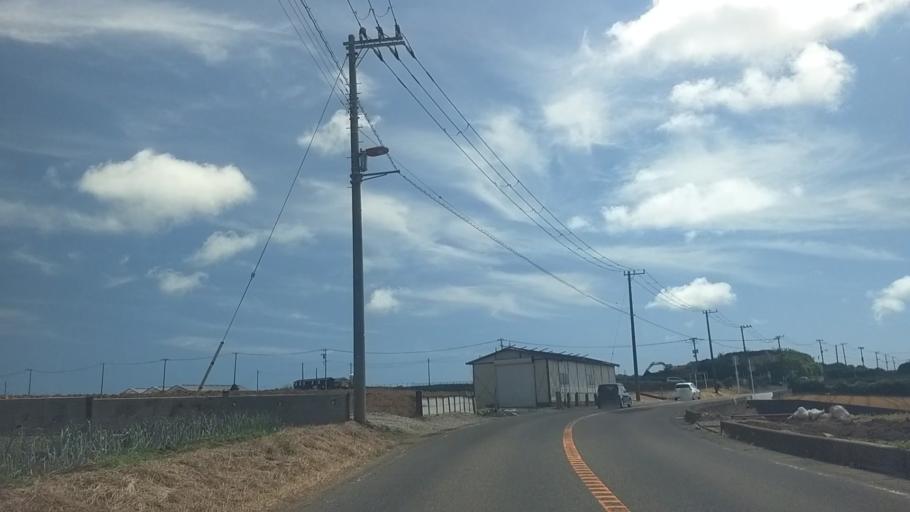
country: JP
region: Kanagawa
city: Miura
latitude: 35.1990
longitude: 139.6513
